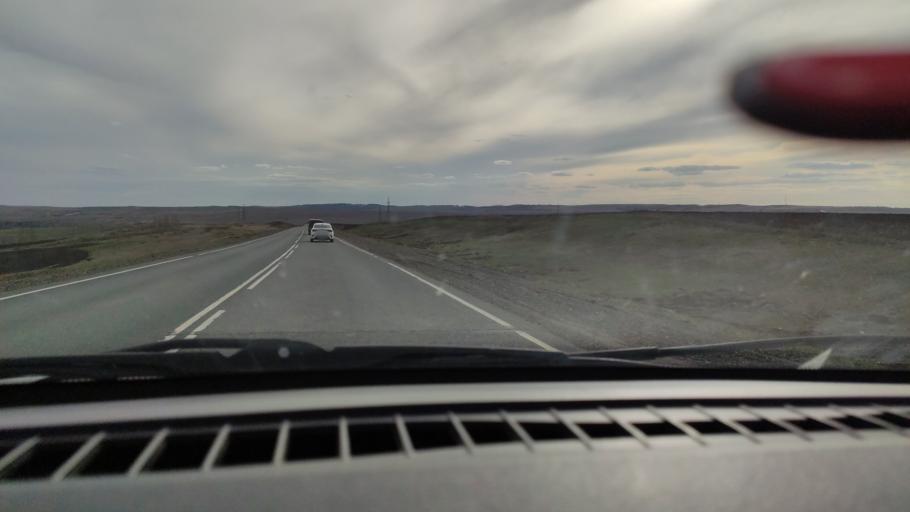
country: RU
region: Bashkortostan
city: Yermolayevo
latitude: 52.6751
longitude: 55.8495
